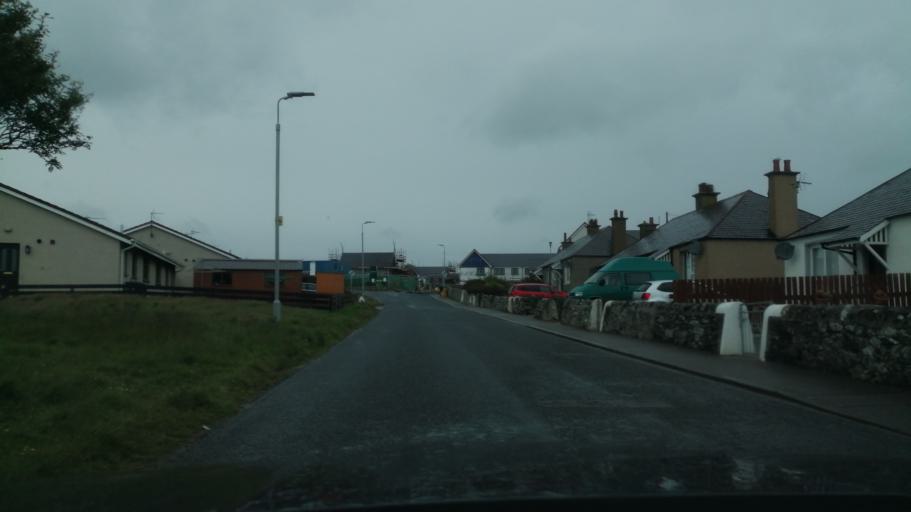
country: GB
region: Scotland
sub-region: Aberdeenshire
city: Portsoy
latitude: 57.6819
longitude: -2.6991
